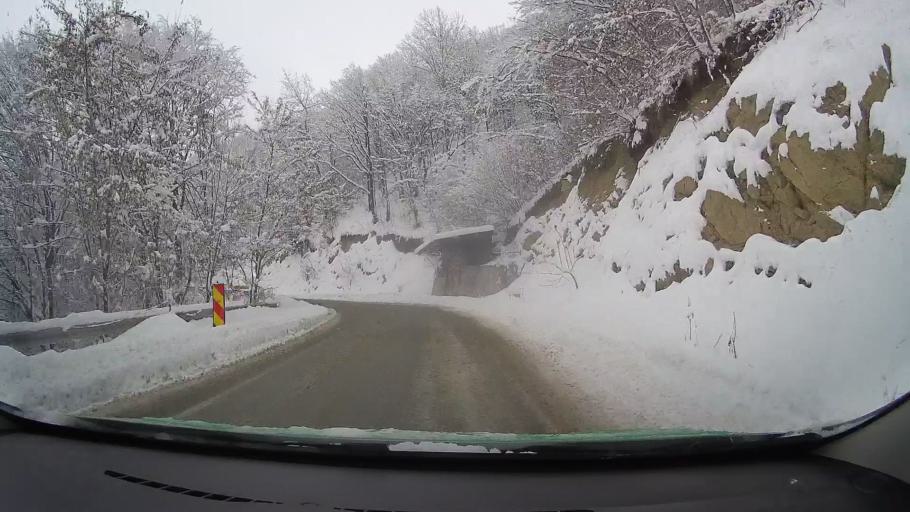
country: RO
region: Sibiu
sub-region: Comuna Jina
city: Jina
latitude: 45.7677
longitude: 23.6698
